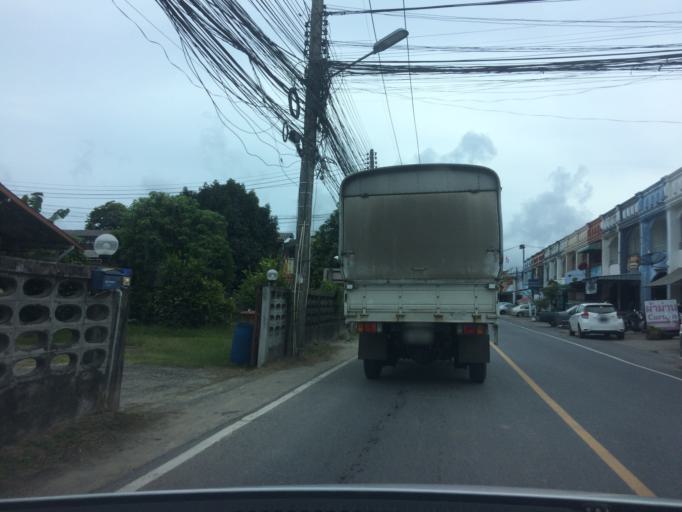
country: TH
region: Phuket
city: Mueang Phuket
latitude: 7.8624
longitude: 98.3664
